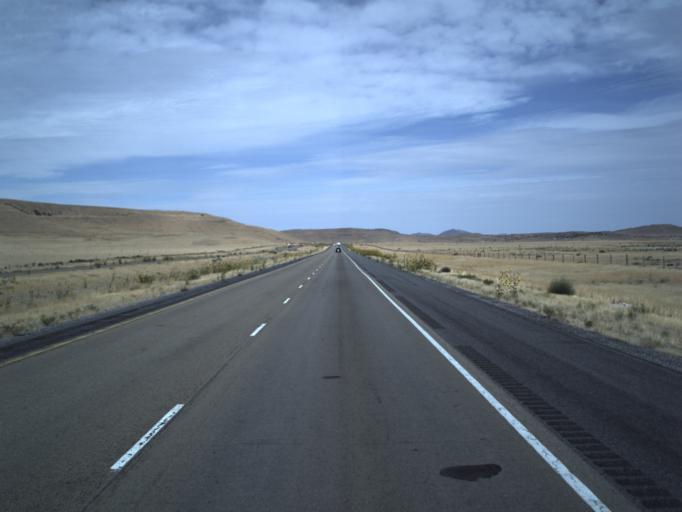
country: US
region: Utah
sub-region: Tooele County
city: Grantsville
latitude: 40.8035
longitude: -112.8555
